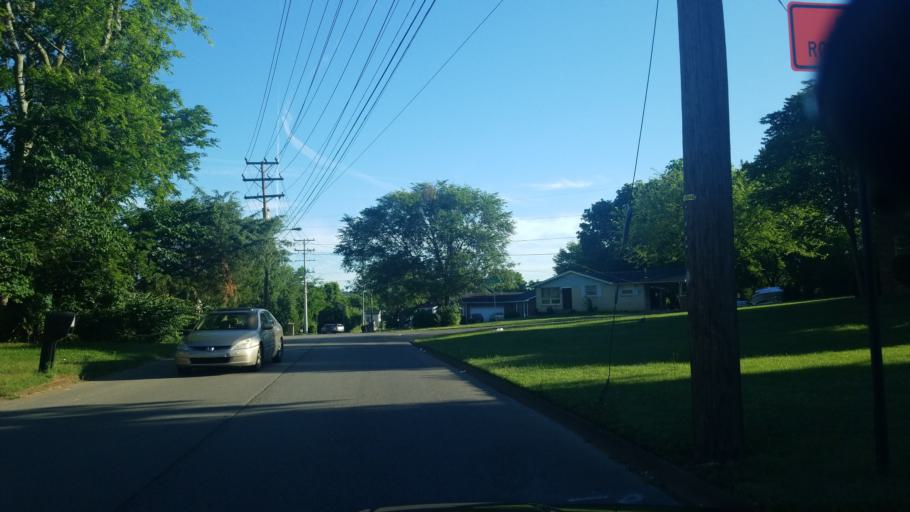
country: US
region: Tennessee
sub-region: Davidson County
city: Nashville
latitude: 36.2408
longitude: -86.7730
